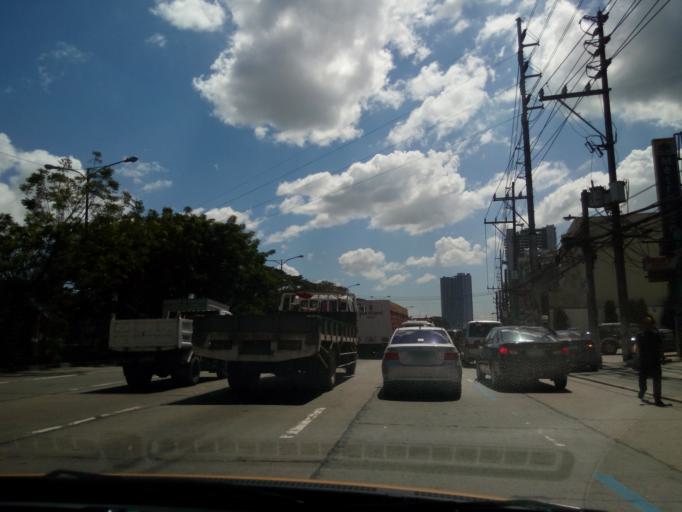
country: PH
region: Metro Manila
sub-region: Quezon City
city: Quezon City
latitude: 14.6443
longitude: 121.0745
